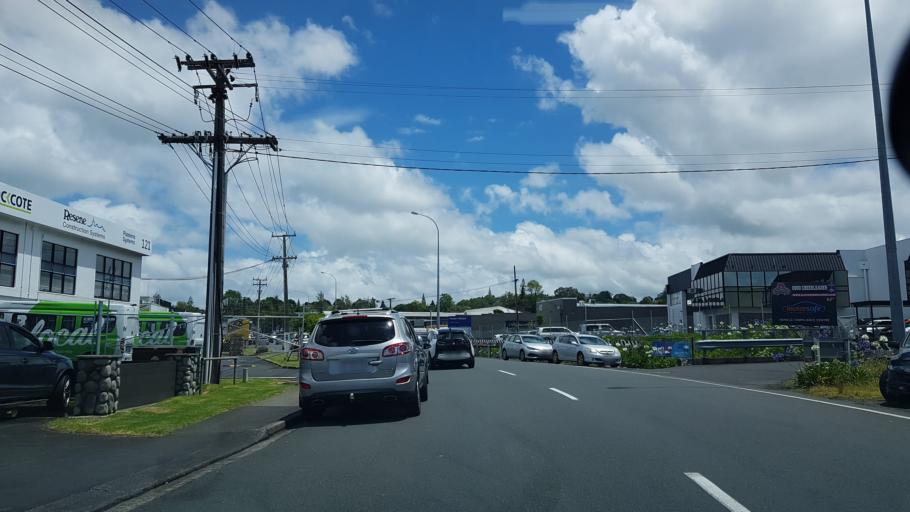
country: NZ
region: Auckland
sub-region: Auckland
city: North Shore
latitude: -36.7739
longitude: 174.7346
